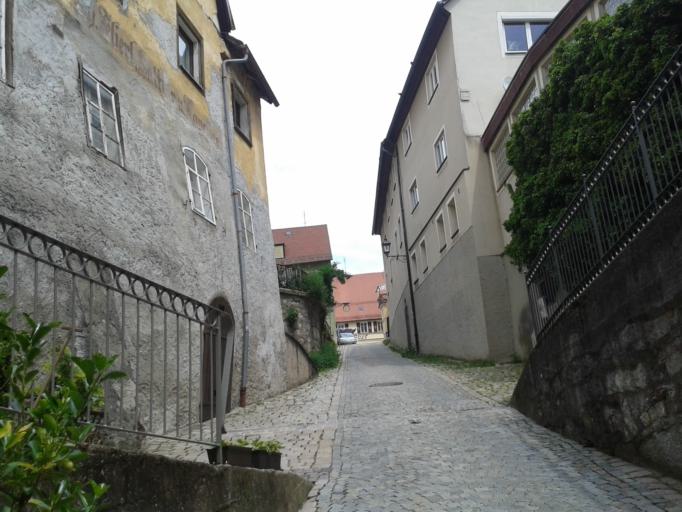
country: DE
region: Bavaria
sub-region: Upper Franconia
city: Grafenberg
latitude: 49.6440
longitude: 11.2490
